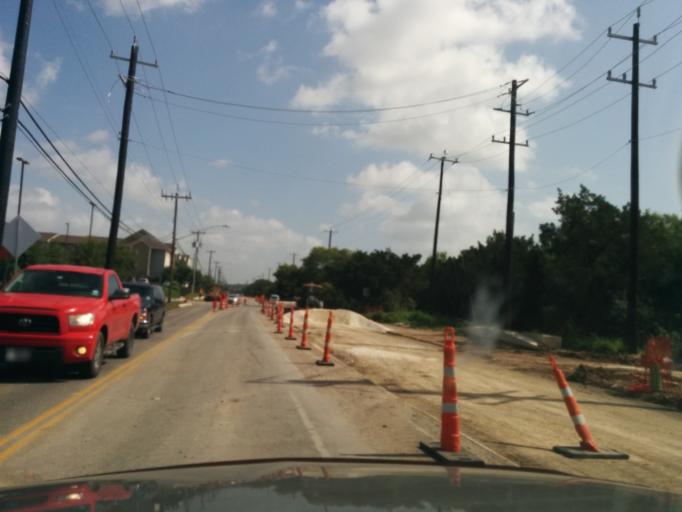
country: US
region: Texas
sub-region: Bexar County
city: Helotes
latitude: 29.5722
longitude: -98.6316
